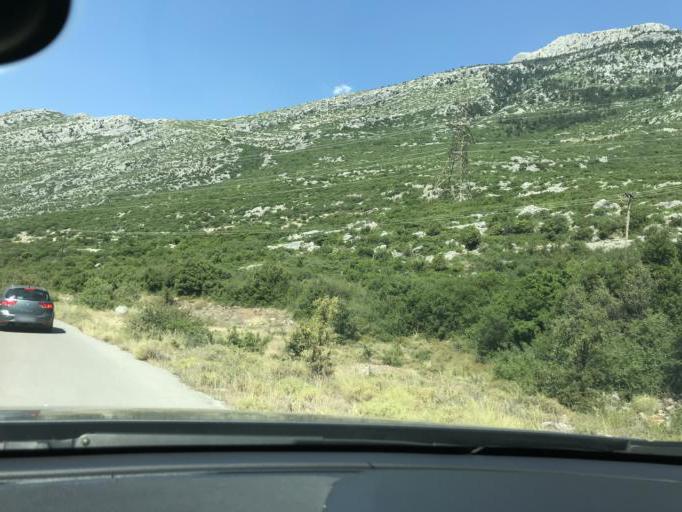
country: GR
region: Central Greece
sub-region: Nomos Voiotias
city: Distomo
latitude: 38.4916
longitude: 22.6940
